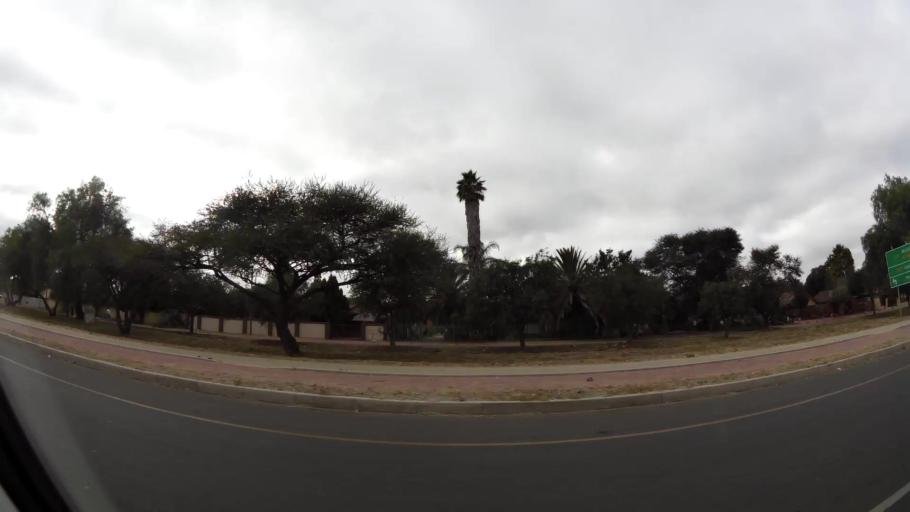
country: ZA
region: Limpopo
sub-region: Capricorn District Municipality
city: Polokwane
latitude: -23.9262
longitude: 29.4515
